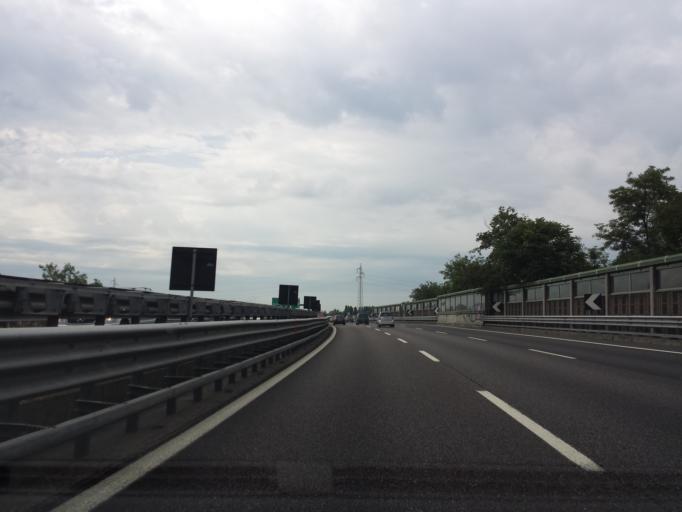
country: IT
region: Lombardy
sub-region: Citta metropolitana di Milano
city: Settimo Milanese
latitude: 45.4643
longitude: 9.0761
